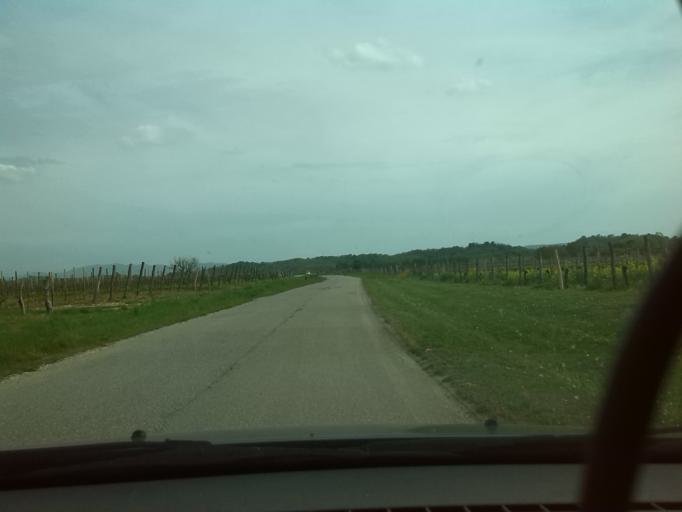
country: SI
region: Brda
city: Dobrovo
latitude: 45.9706
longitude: 13.5205
